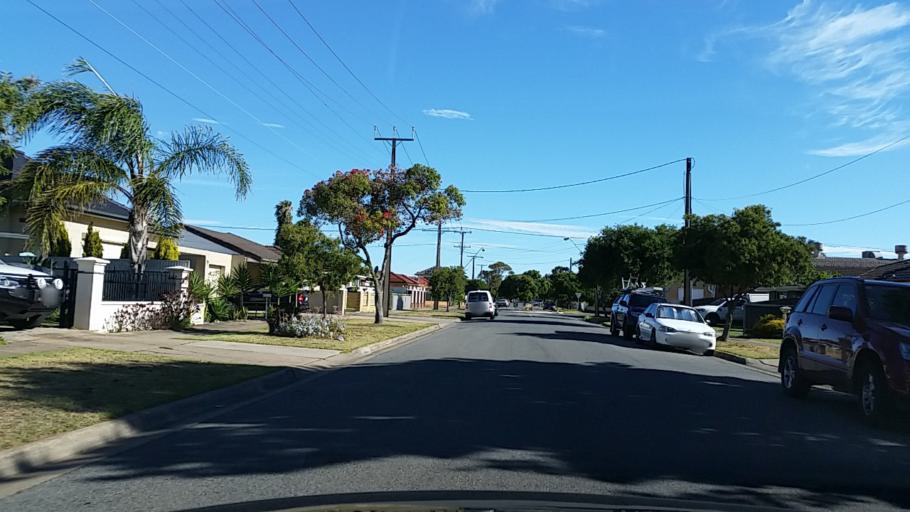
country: AU
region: South Australia
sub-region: Charles Sturt
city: Royal Park
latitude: -34.8714
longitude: 138.5105
